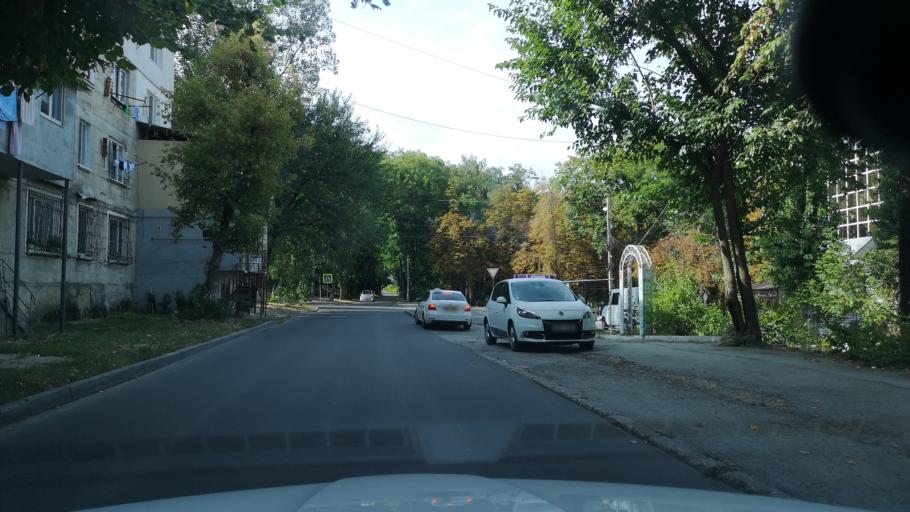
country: MD
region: Chisinau
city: Chisinau
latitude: 47.0349
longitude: 28.8046
